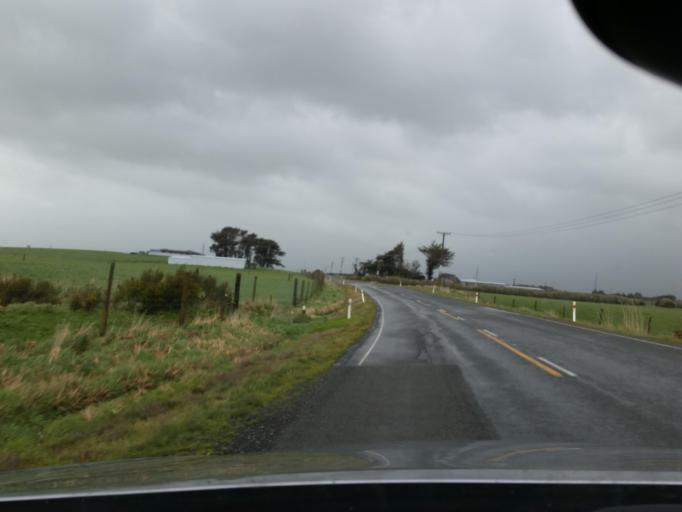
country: NZ
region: Southland
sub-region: Invercargill City
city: Invercargill
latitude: -46.4515
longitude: 168.4228
